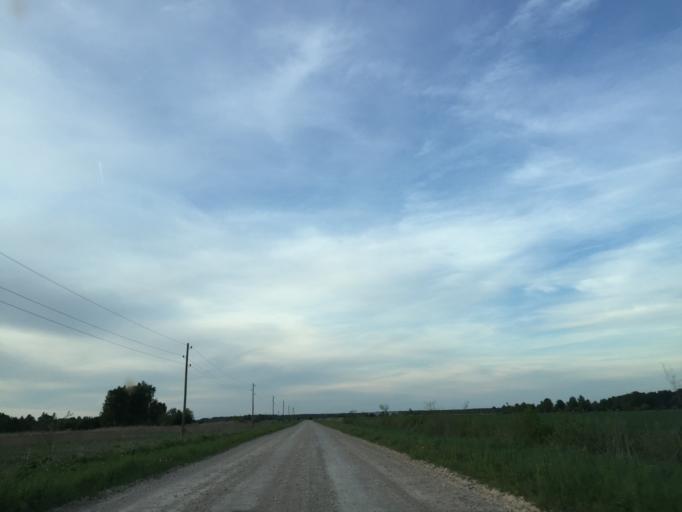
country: LV
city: Tireli
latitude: 56.7965
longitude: 23.5677
